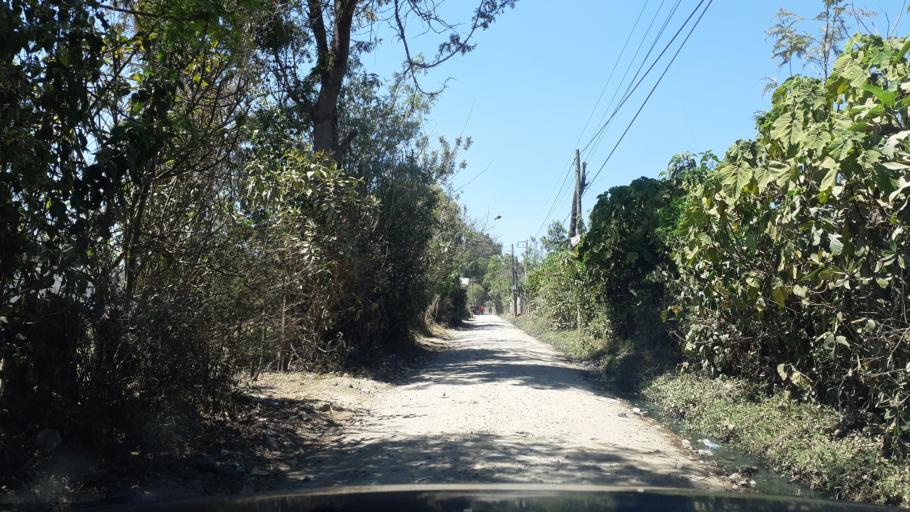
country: GT
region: Chimaltenango
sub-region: Municipio de Chimaltenango
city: Chimaltenango
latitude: 14.6519
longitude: -90.8087
